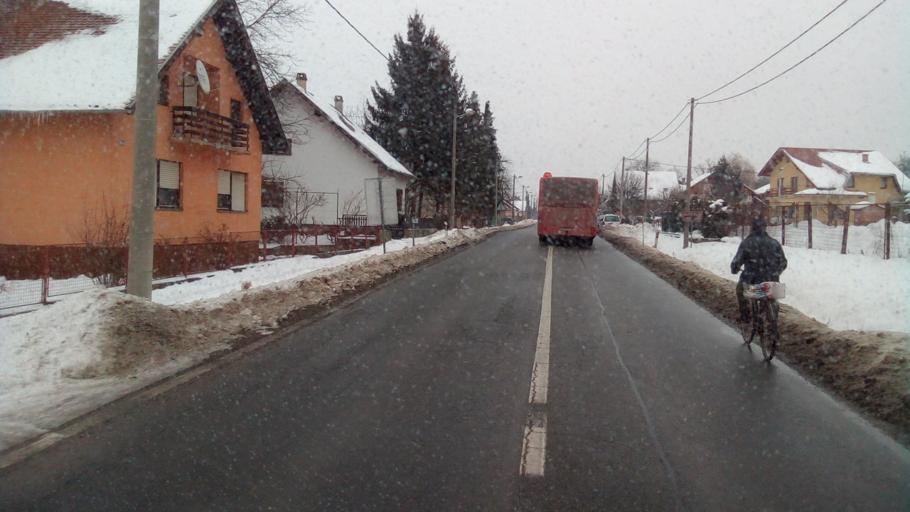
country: HR
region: Sisacko-Moslavacka
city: Petrinja
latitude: 45.4435
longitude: 16.3181
